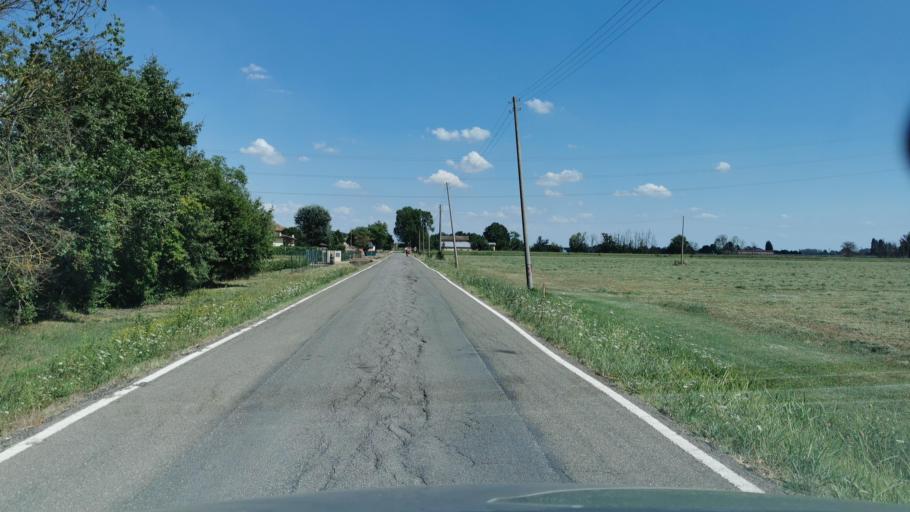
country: IT
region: Emilia-Romagna
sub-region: Provincia di Modena
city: Limidi
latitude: 44.7841
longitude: 10.9107
